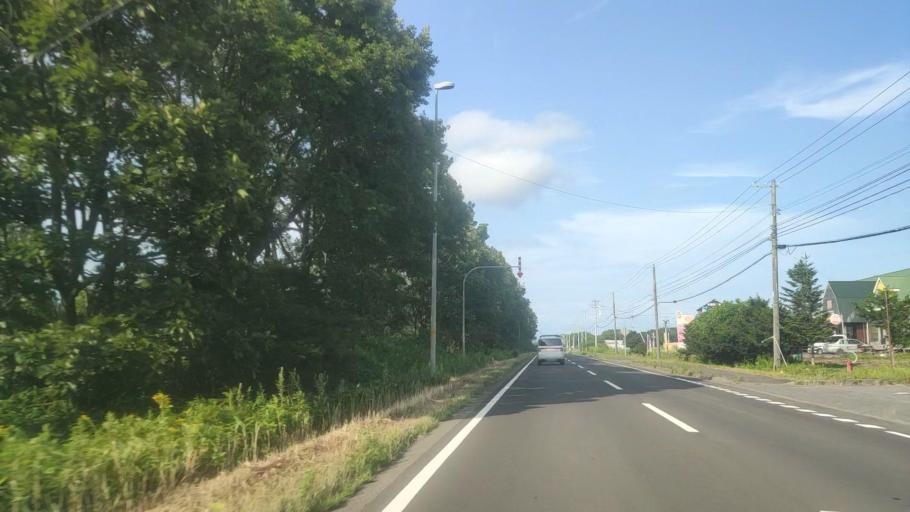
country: JP
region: Hokkaido
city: Chitose
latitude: 42.7412
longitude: 141.7844
